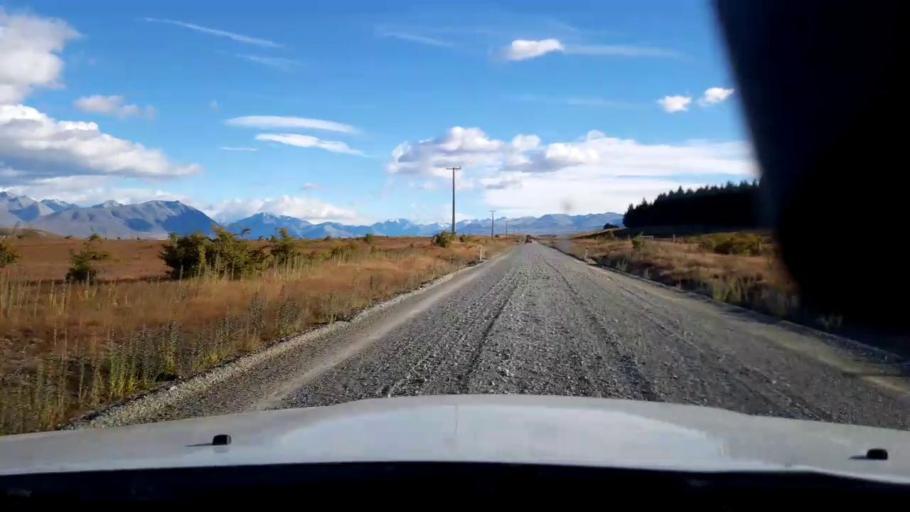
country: NZ
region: Canterbury
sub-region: Timaru District
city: Pleasant Point
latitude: -43.9850
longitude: 170.5063
